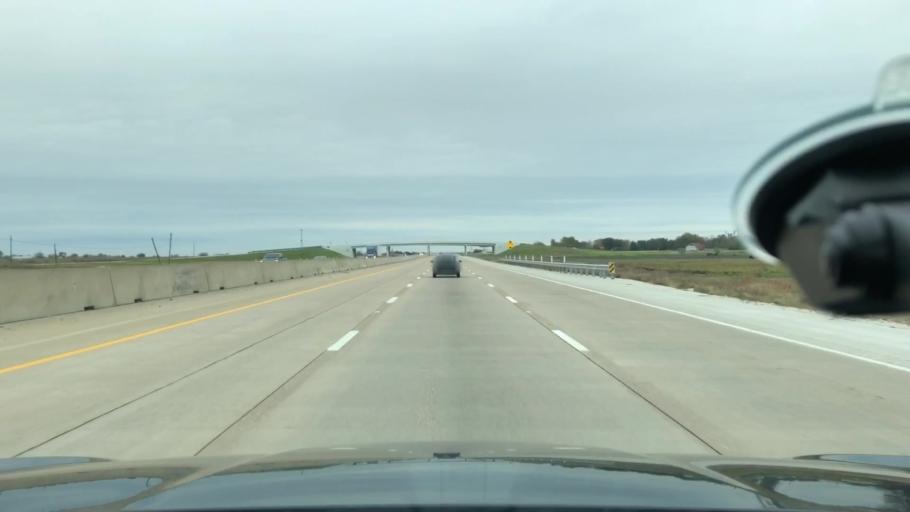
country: US
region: Texas
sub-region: Ellis County
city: Waxahachie
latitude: 32.3190
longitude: -96.8607
